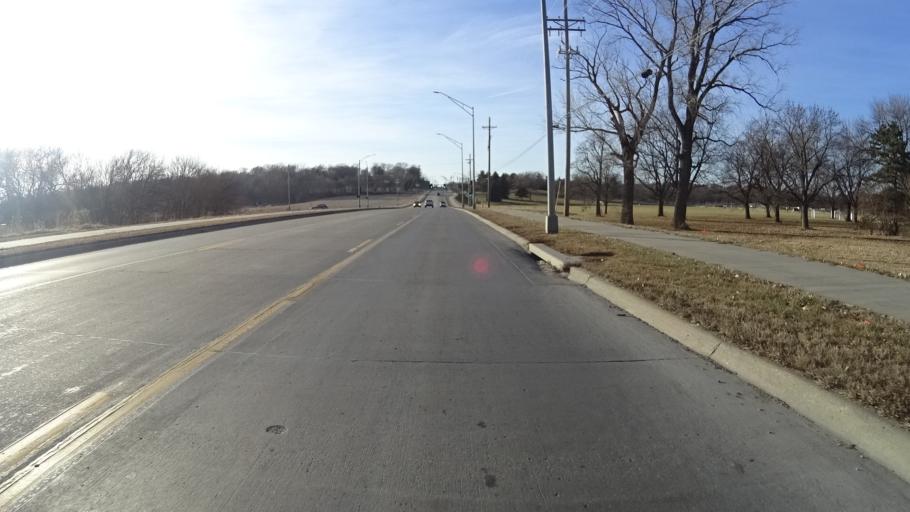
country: US
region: Nebraska
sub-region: Sarpy County
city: La Vista
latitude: 41.1908
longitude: -96.0123
